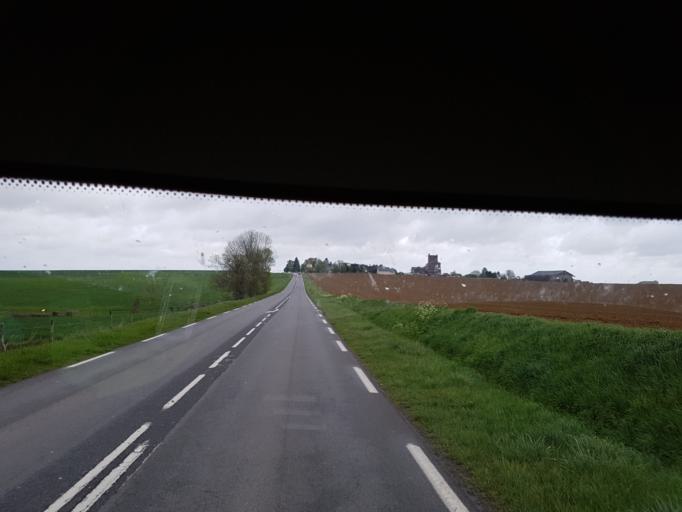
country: FR
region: Picardie
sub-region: Departement de l'Aisne
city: Crouy
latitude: 49.4404
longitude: 3.3570
